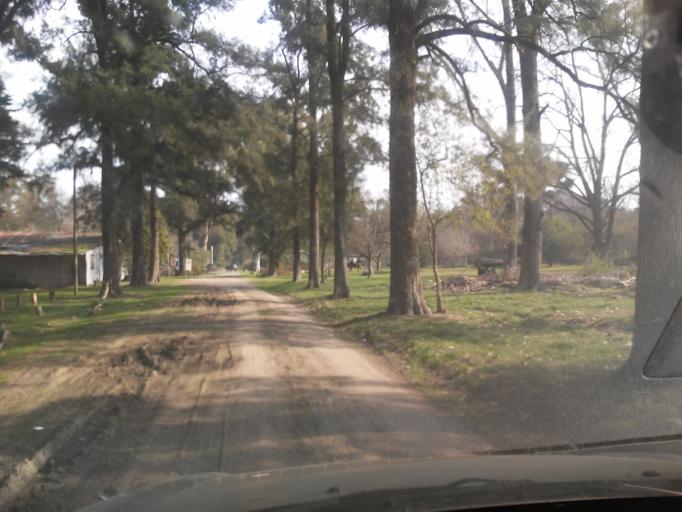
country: AR
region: Buenos Aires
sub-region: Partido de General Rodriguez
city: General Rodriguez
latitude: -34.6646
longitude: -58.8598
